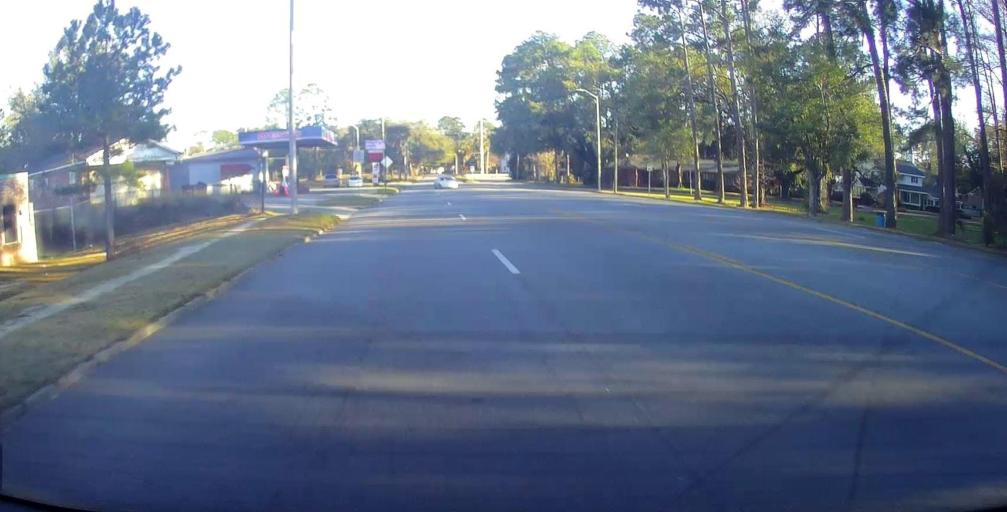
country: US
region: Georgia
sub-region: Dougherty County
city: Albany
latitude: 31.5964
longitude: -84.1629
